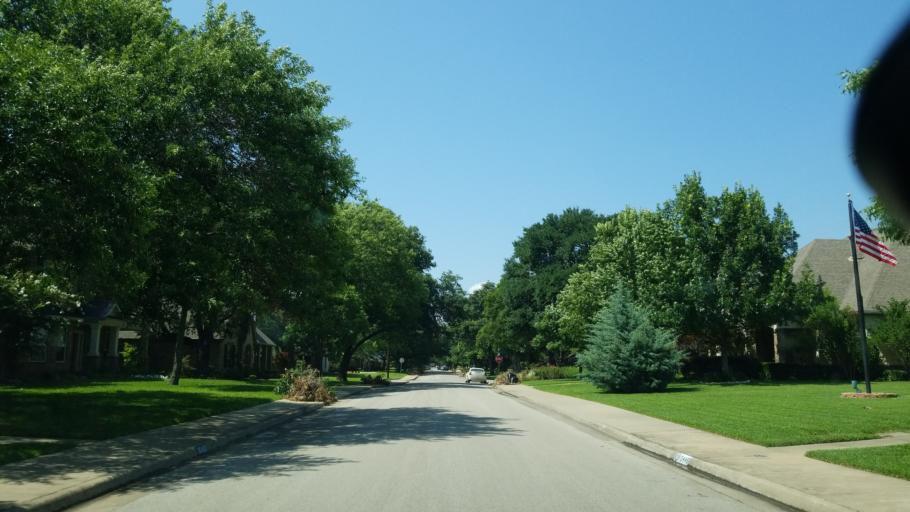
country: US
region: Texas
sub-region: Dallas County
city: Farmers Branch
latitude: 32.8890
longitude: -96.8639
